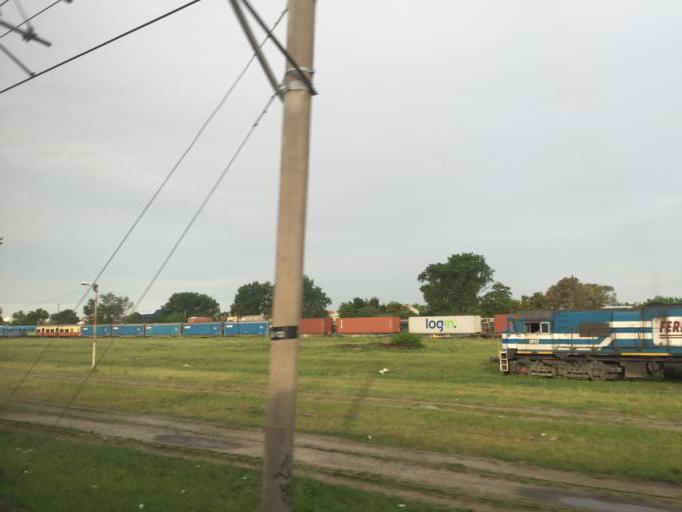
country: AR
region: Buenos Aires
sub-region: Partido de Lanus
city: Lanus
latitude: -34.6841
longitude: -58.3820
